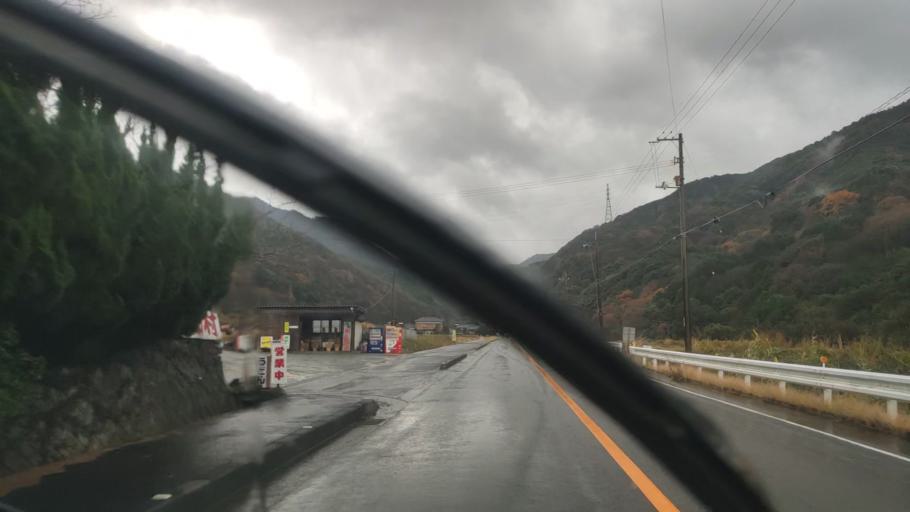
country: JP
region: Tokushima
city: Kamojimacho-jogejima
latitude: 34.1954
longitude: 134.3329
